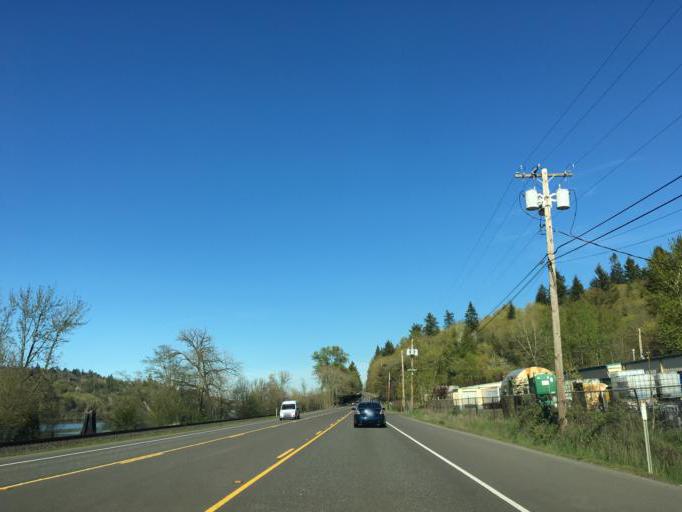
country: US
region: Oregon
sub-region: Clackamas County
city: Oregon City
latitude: 45.3411
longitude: -122.6370
